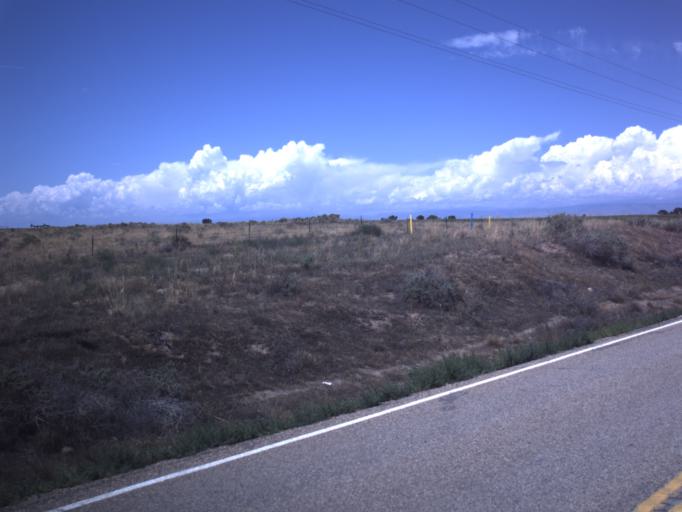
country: US
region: Utah
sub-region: Uintah County
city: Naples
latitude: 40.1348
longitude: -109.6639
